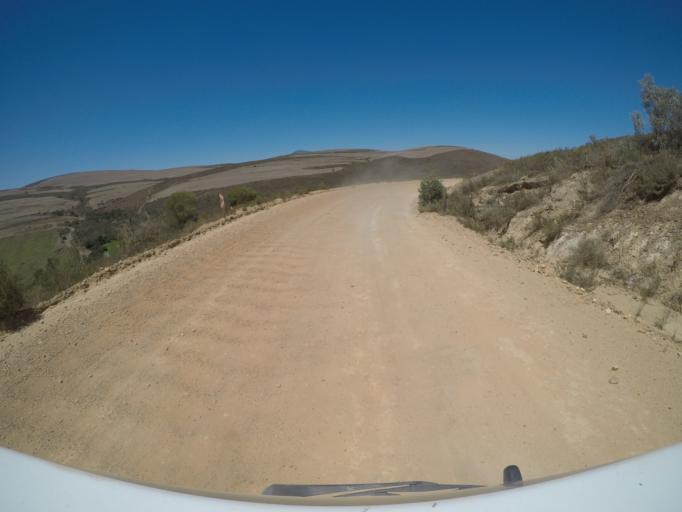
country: ZA
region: Western Cape
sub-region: Overberg District Municipality
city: Grabouw
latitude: -34.2054
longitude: 19.2160
